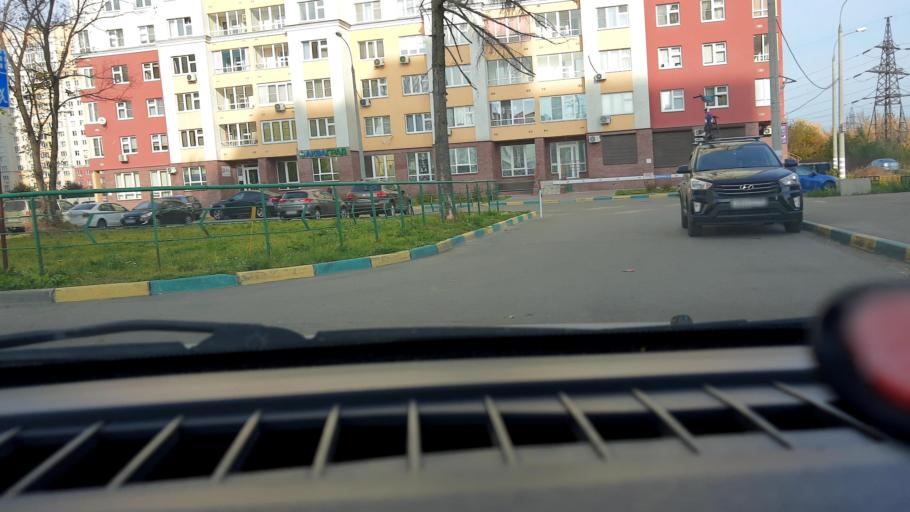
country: RU
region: Nizjnij Novgorod
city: Neklyudovo
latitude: 56.3464
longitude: 43.8733
